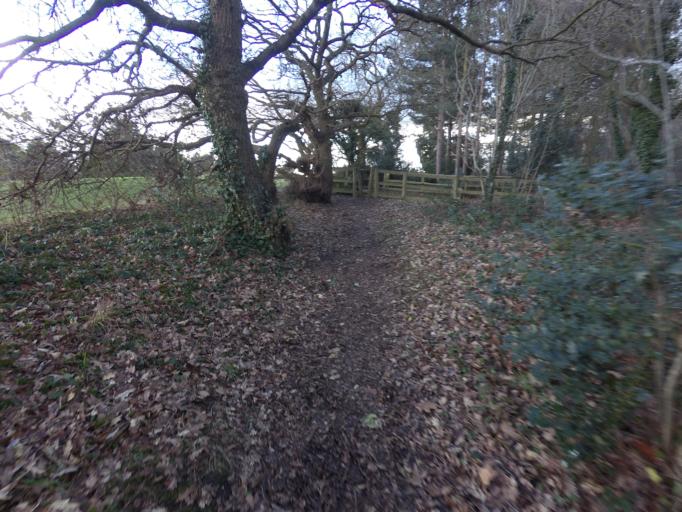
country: GB
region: England
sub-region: Kent
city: Swanley
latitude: 51.4180
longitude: 0.1597
